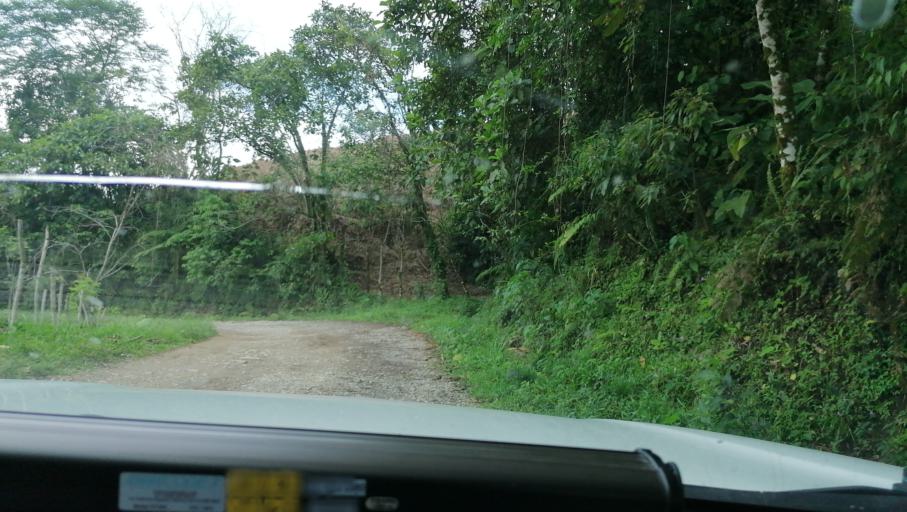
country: MX
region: Chiapas
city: Ocotepec
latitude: 17.3256
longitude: -93.1323
